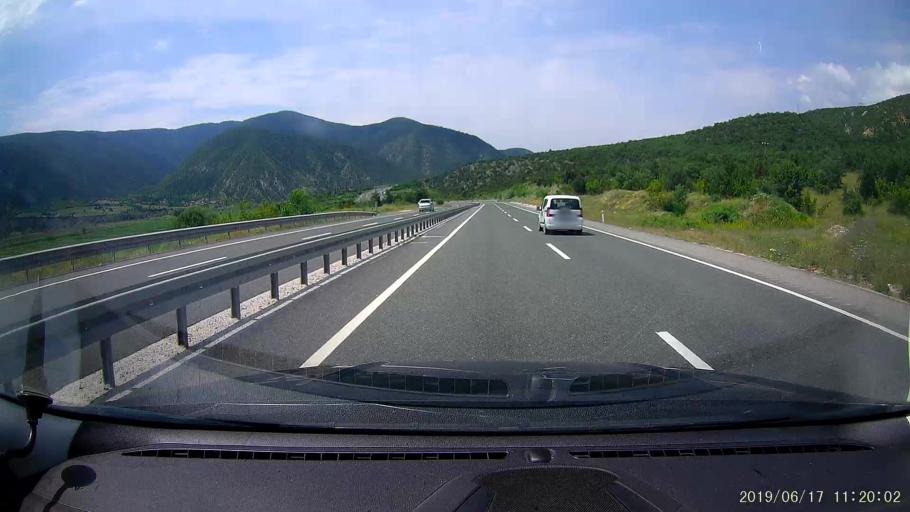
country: TR
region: Cankiri
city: Yaprakli
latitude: 40.9186
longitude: 33.8152
